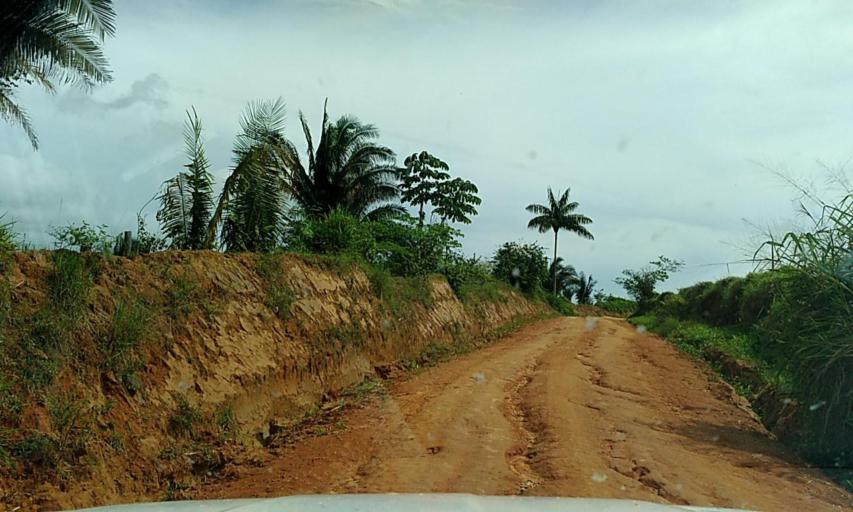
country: BR
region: Para
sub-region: Altamira
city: Altamira
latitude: -3.2260
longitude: -52.7457
